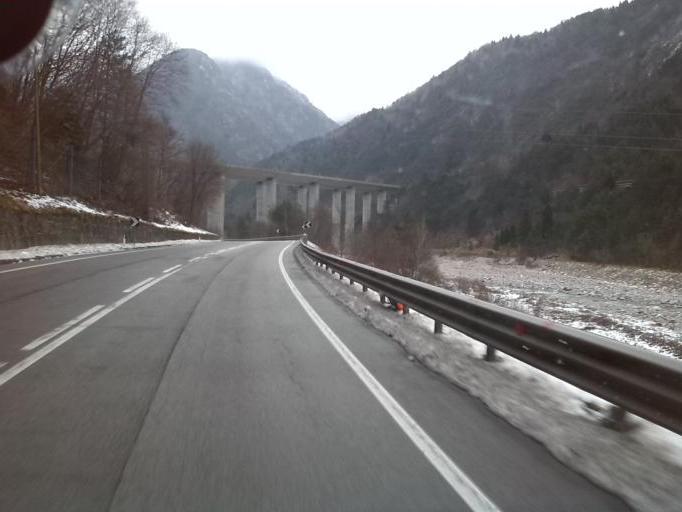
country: IT
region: Friuli Venezia Giulia
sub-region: Provincia di Udine
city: Dogna
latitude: 46.4545
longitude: 13.3078
